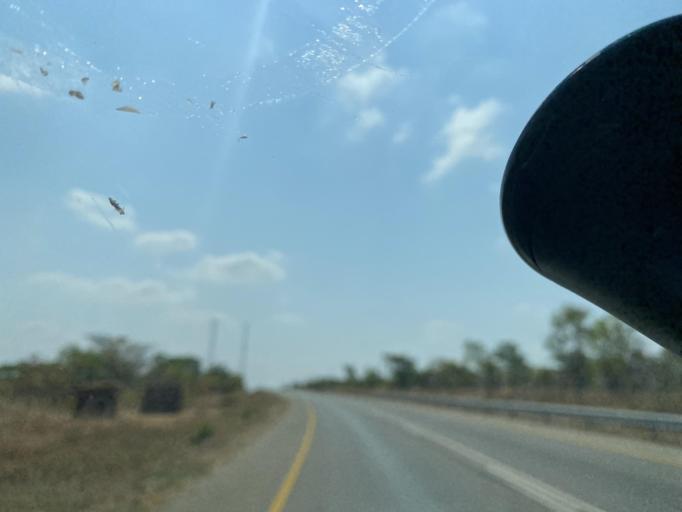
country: ZM
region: Lusaka
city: Chongwe
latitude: -15.5310
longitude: 28.6361
